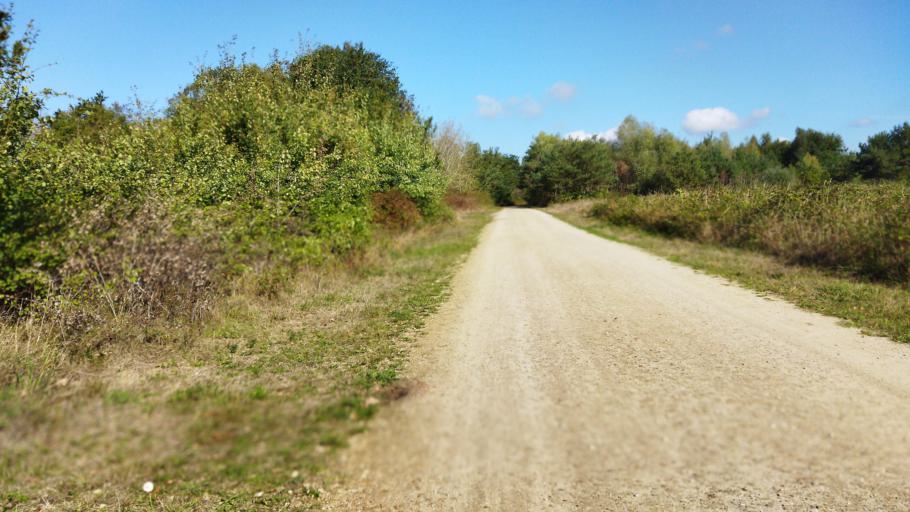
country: DE
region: Lower Saxony
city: Ohne
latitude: 52.2740
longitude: 7.3142
